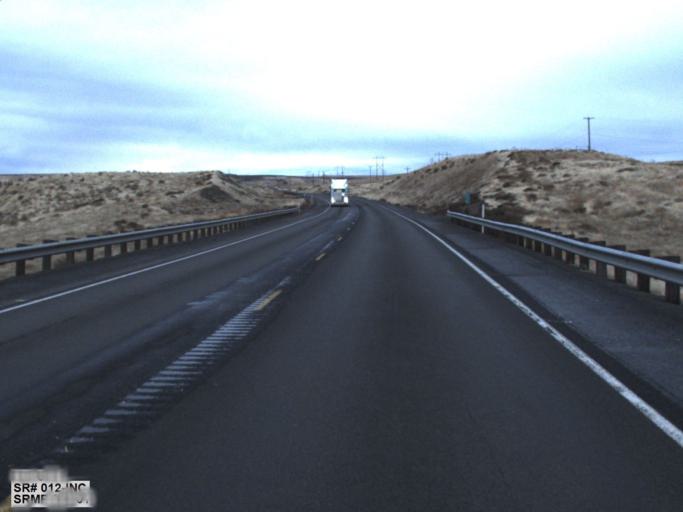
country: US
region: Washington
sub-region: Benton County
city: Finley
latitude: 46.0556
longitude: -118.8597
